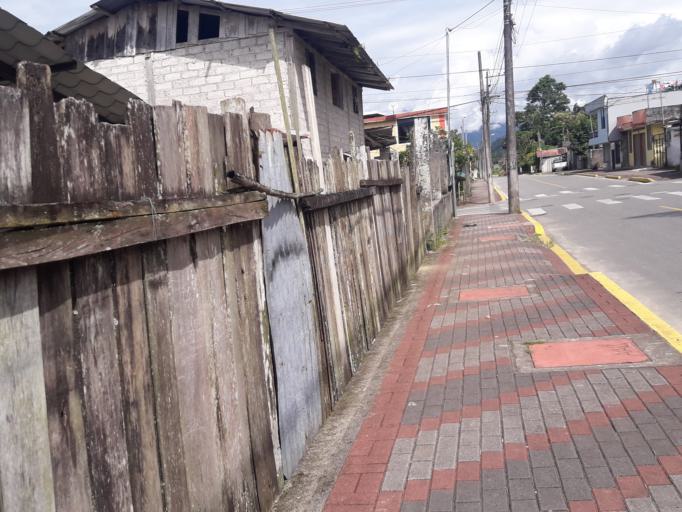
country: EC
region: Napo
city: Tena
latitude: -1.0061
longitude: -77.8151
